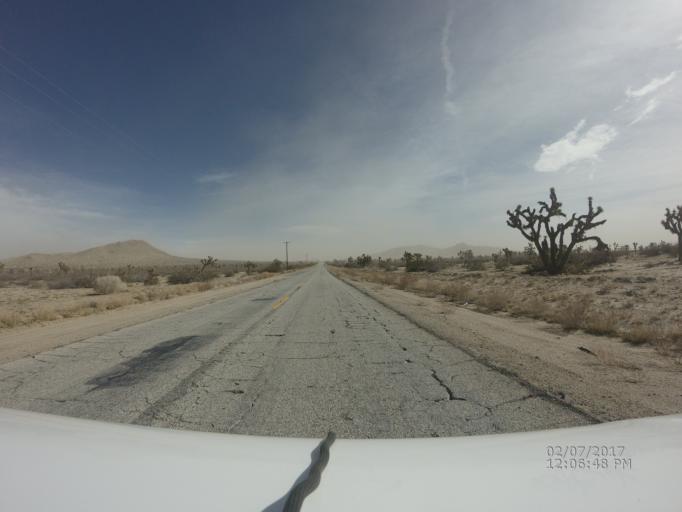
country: US
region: California
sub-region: Los Angeles County
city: Lake Los Angeles
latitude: 34.6900
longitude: -117.8435
